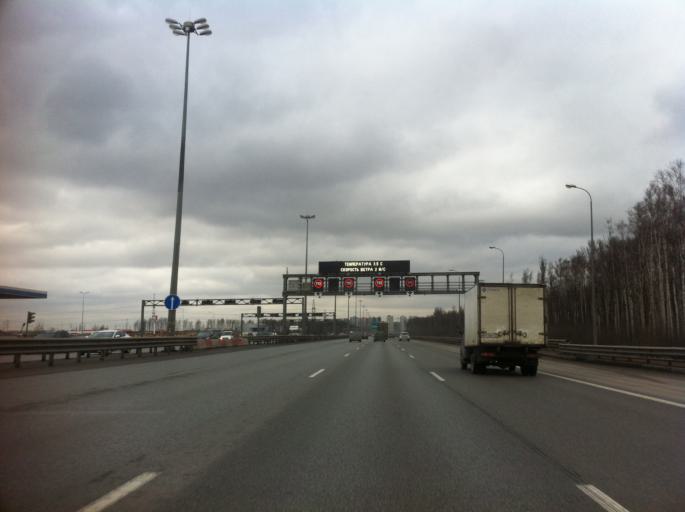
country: RU
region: Leningrad
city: Rybatskoye
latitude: 59.8763
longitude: 30.5306
